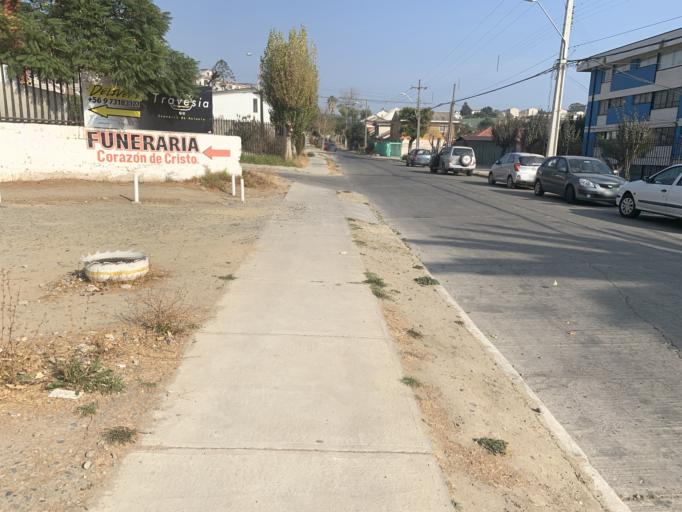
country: CL
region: Valparaiso
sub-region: Provincia de Marga Marga
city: Quilpue
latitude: -33.0498
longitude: -71.4345
